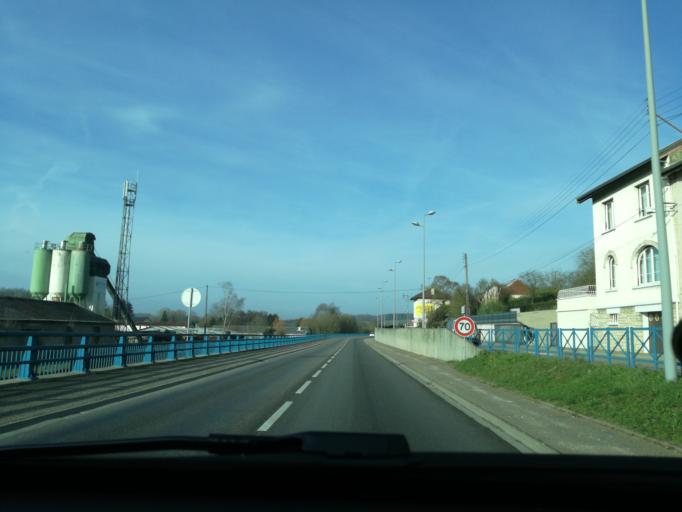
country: FR
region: Lorraine
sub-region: Departement de la Meuse
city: Bar-le-Duc
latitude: 48.7812
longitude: 5.1568
